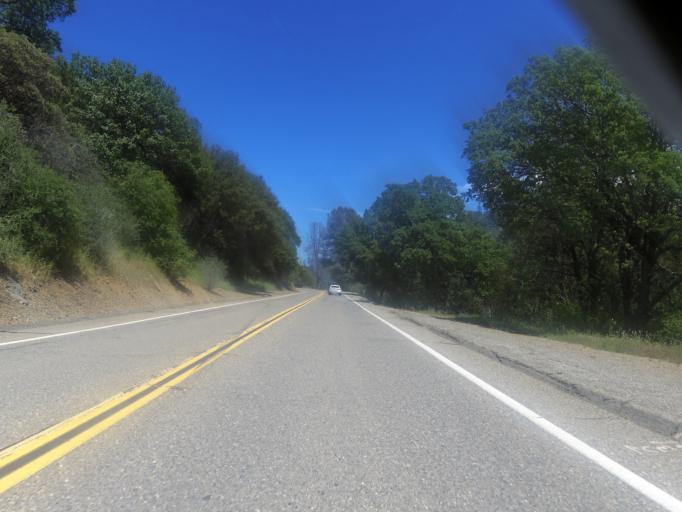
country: US
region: California
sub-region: Mariposa County
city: Mariposa
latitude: 37.5139
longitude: -119.9601
